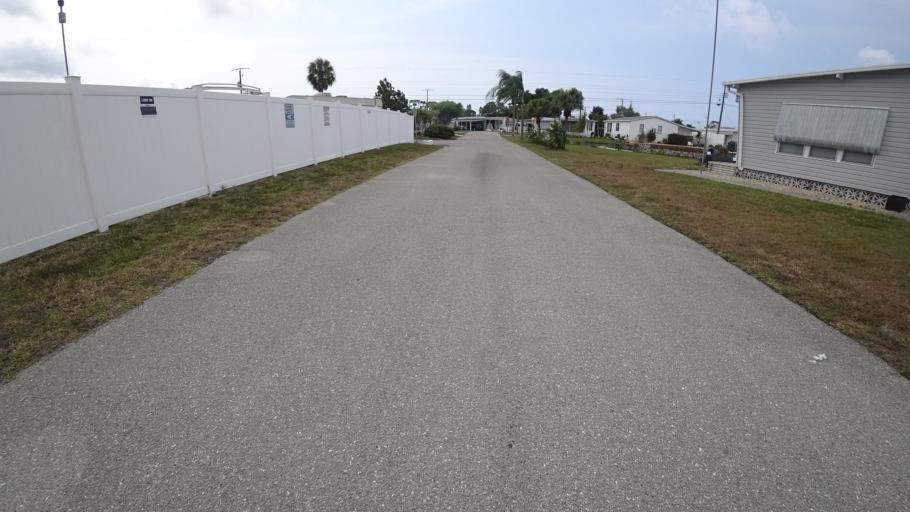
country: US
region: Florida
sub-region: Manatee County
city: West Samoset
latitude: 27.4503
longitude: -82.5644
